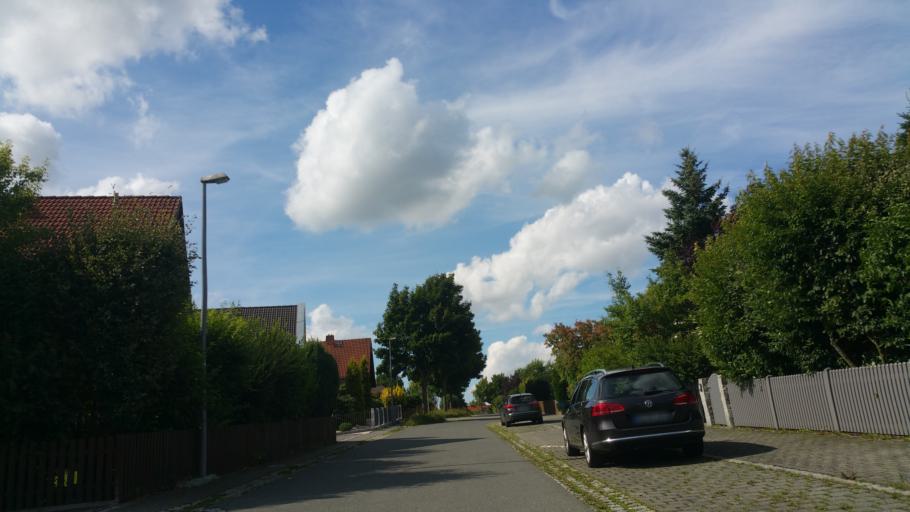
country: DE
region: Bavaria
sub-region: Upper Franconia
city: Oberkotzau
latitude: 50.2541
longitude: 11.9283
